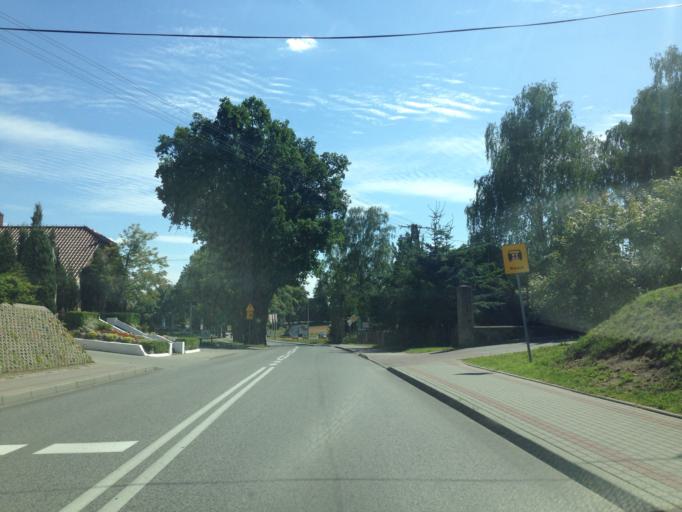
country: PL
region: Kujawsko-Pomorskie
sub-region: Powiat swiecki
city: Osie
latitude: 53.5972
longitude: 18.3476
